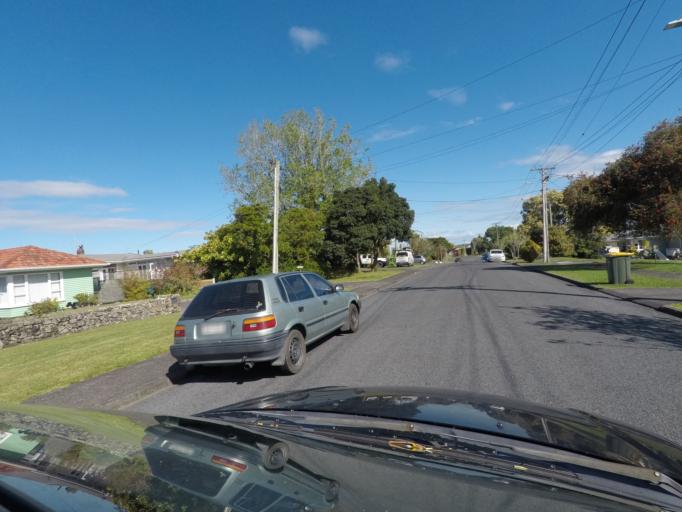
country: NZ
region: Auckland
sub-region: Auckland
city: Rosebank
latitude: -36.8616
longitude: 174.6545
